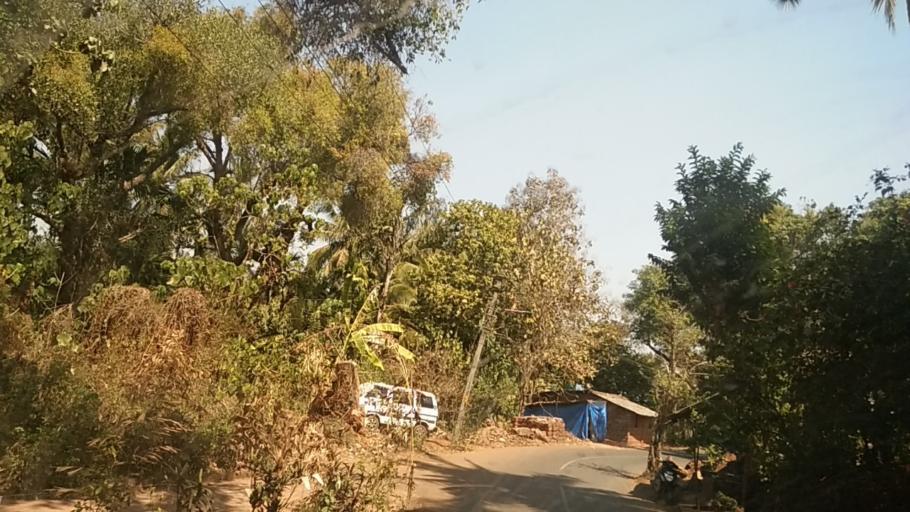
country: IN
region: Goa
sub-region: North Goa
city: Aldona
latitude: 15.5752
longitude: 73.9071
